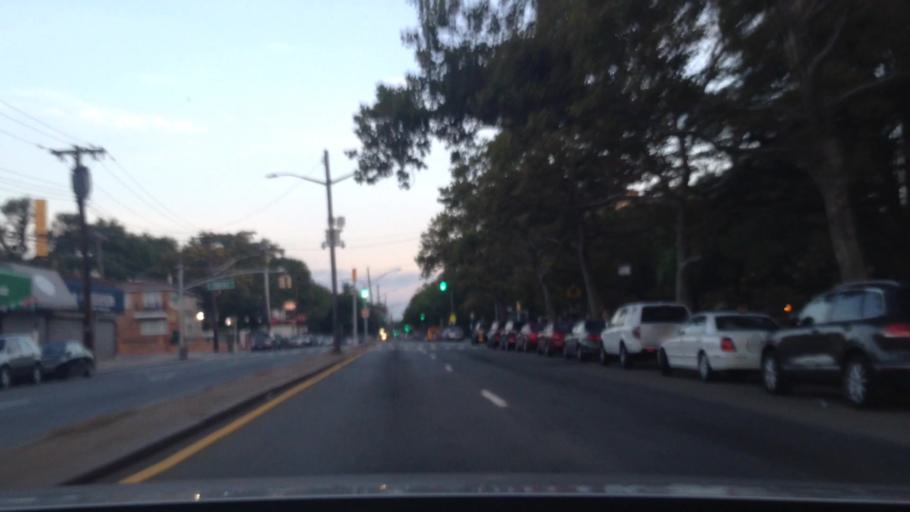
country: US
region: New York
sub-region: Queens County
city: Jamaica
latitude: 40.6728
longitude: -73.7752
